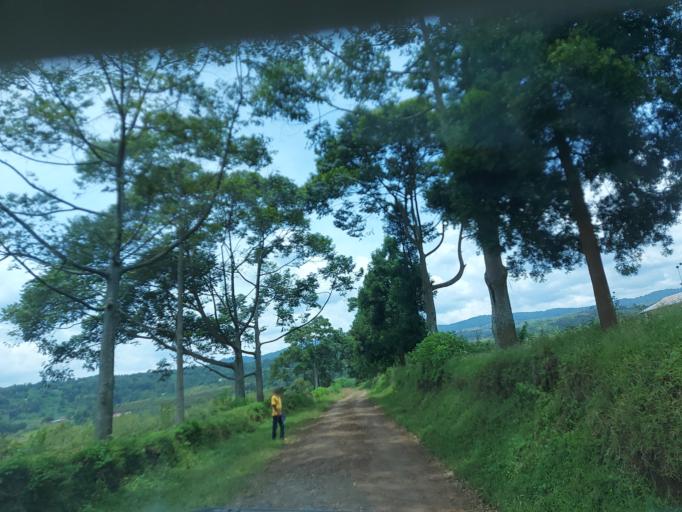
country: CD
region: South Kivu
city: Kabare
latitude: -2.3384
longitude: 28.7877
